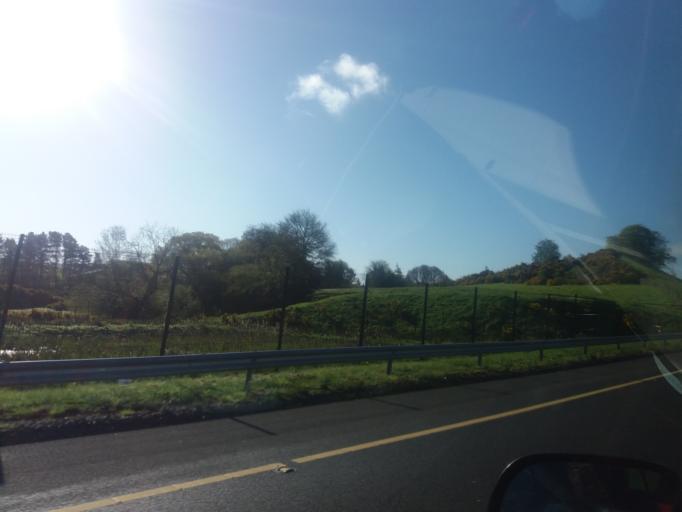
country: IE
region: Leinster
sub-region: Wicklow
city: Rathnew
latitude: 52.9299
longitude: -6.1237
